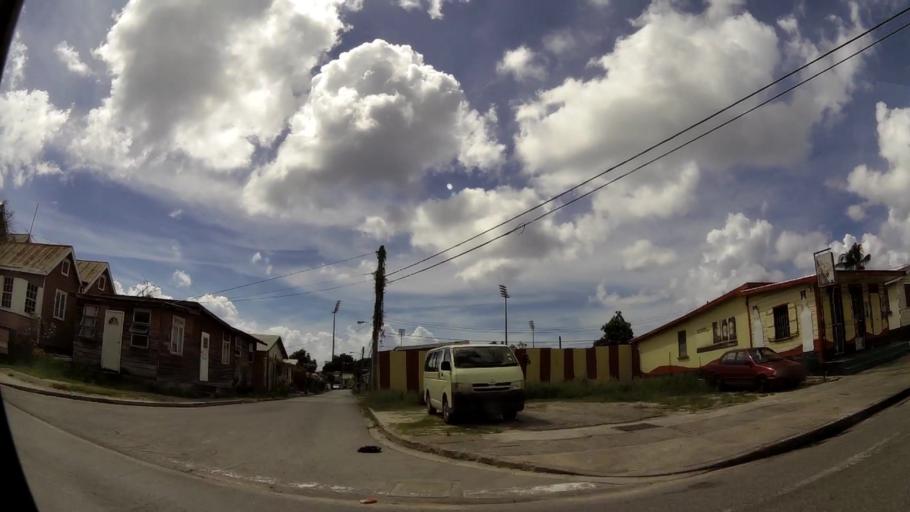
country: BB
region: Saint Michael
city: Bridgetown
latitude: 13.1067
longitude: -59.6199
